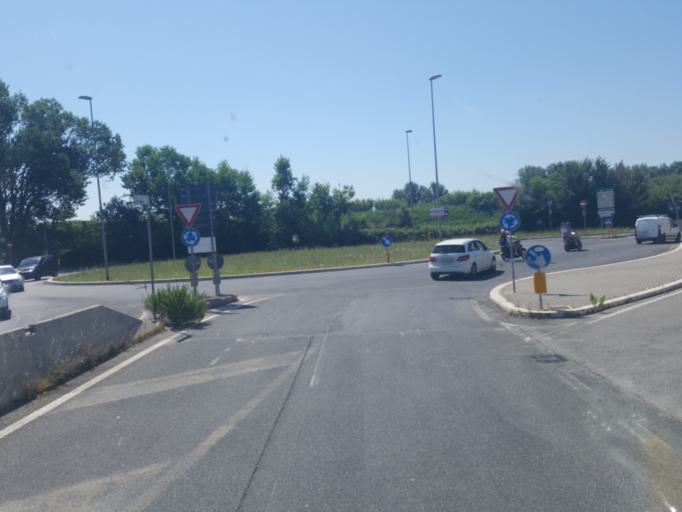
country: IT
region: Latium
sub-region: Citta metropolitana di Roma Capitale
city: Npp 23 (Parco Leonardo)
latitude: 41.7994
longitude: 12.3035
